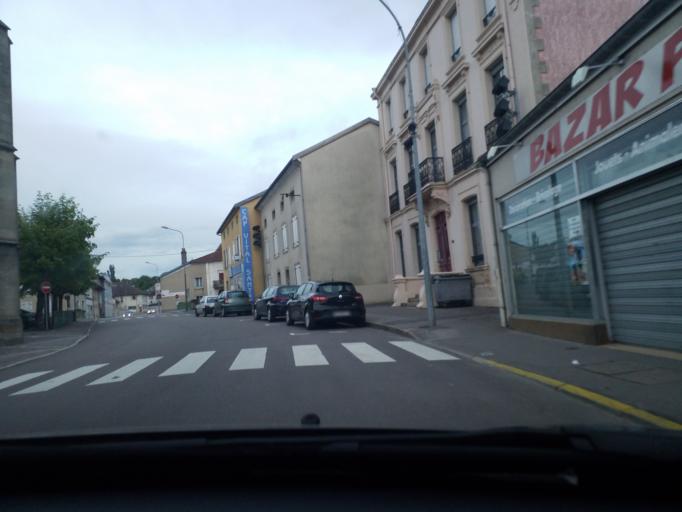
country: FR
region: Lorraine
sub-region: Departement des Vosges
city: Vittel
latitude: 48.1996
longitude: 5.9503
